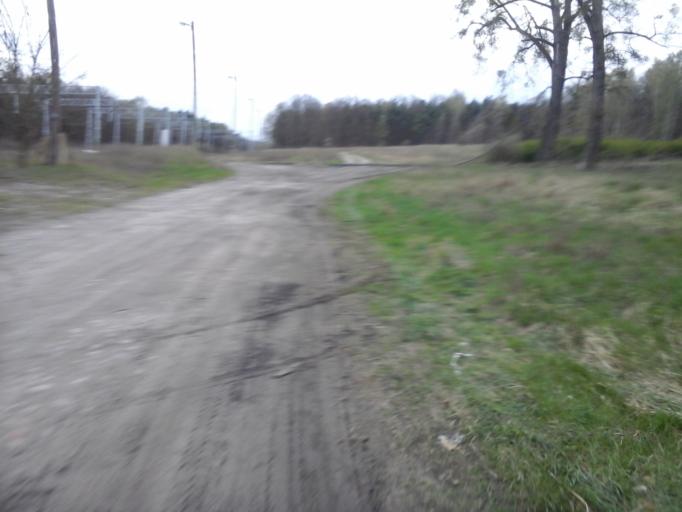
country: PL
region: West Pomeranian Voivodeship
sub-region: Powiat choszczenski
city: Bierzwnik
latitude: 53.0258
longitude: 15.6551
